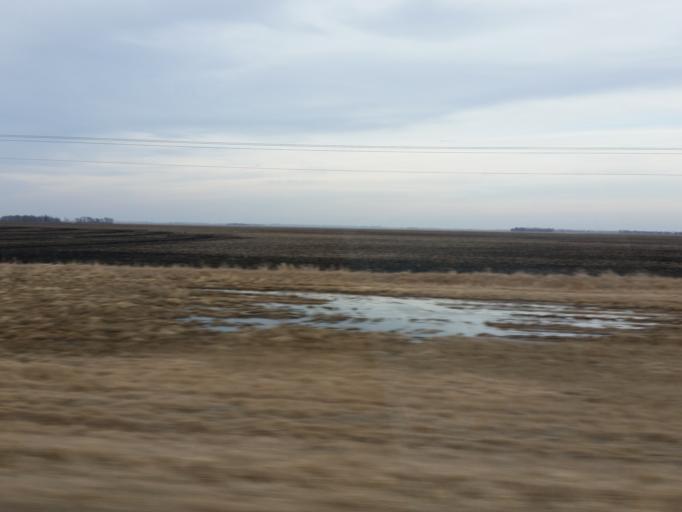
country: US
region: North Dakota
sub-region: Cass County
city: Casselton
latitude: 47.1702
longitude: -97.2174
